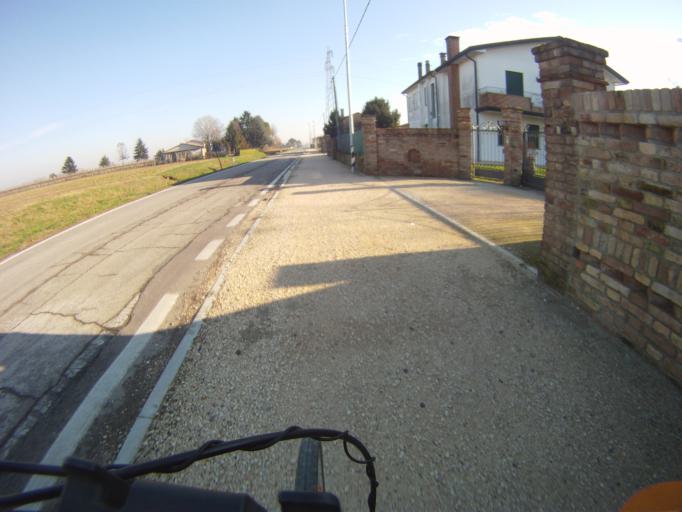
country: IT
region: Veneto
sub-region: Provincia di Padova
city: Polverara
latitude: 45.3135
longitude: 11.9727
